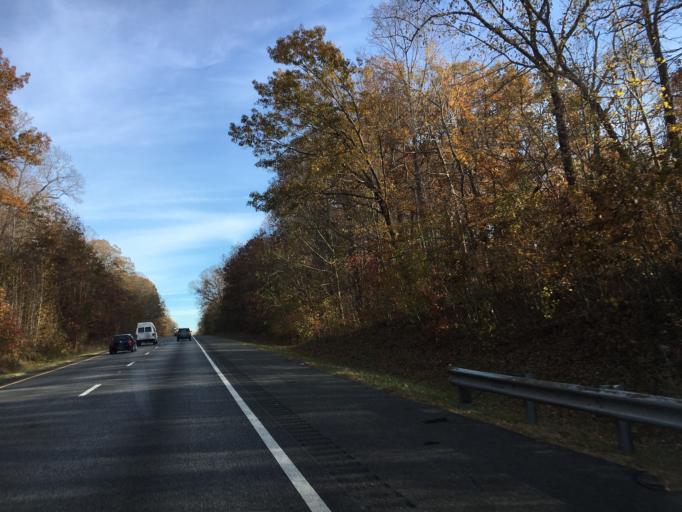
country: US
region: South Carolina
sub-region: Spartanburg County
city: Landrum
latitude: 35.1753
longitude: -82.1483
